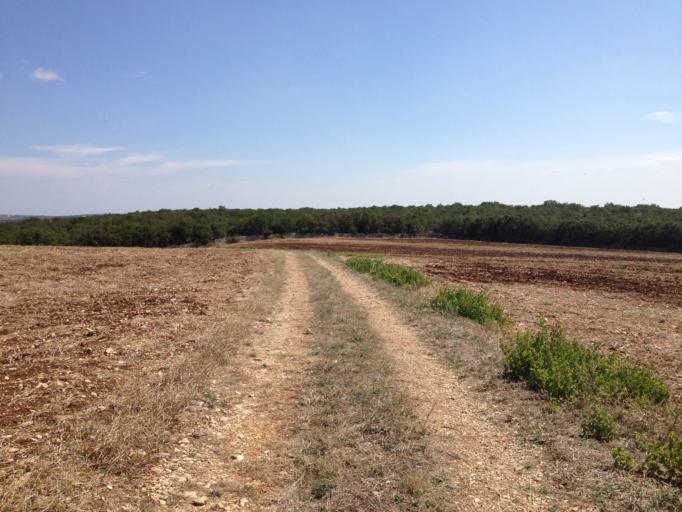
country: IT
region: Apulia
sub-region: Provincia di Bari
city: Gioia del Colle
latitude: 40.8224
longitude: 16.9978
